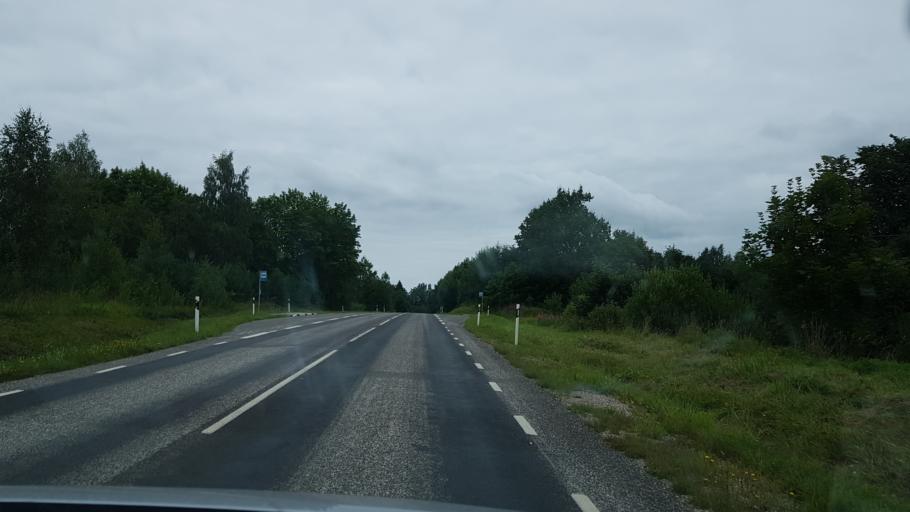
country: EE
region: Vorumaa
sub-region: Antsla vald
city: Vana-Antsla
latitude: 58.0110
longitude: 26.5978
